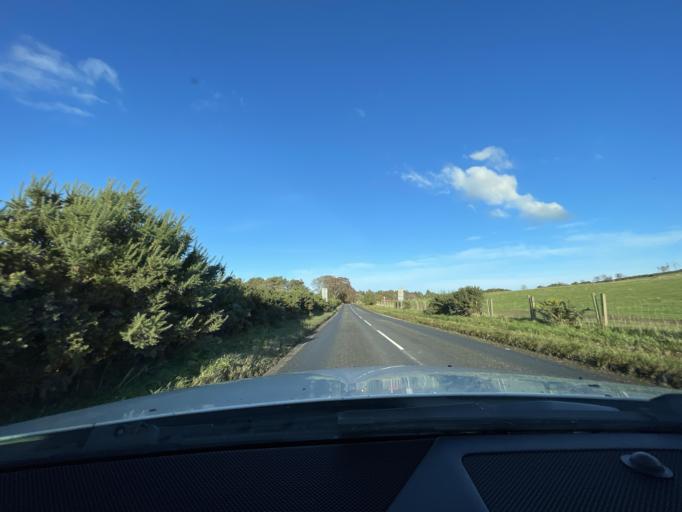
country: GB
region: Scotland
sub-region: Highland
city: Inverness
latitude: 57.3880
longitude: -4.3283
